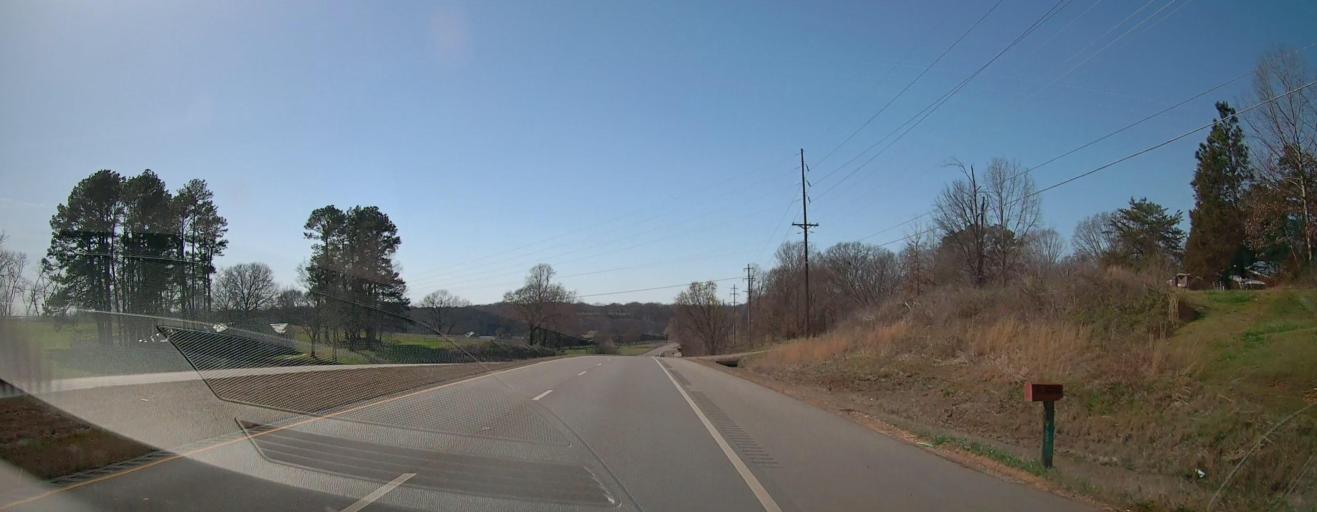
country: US
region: Alabama
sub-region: Lauderdale County
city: Rogersville
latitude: 34.8526
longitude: -87.4038
